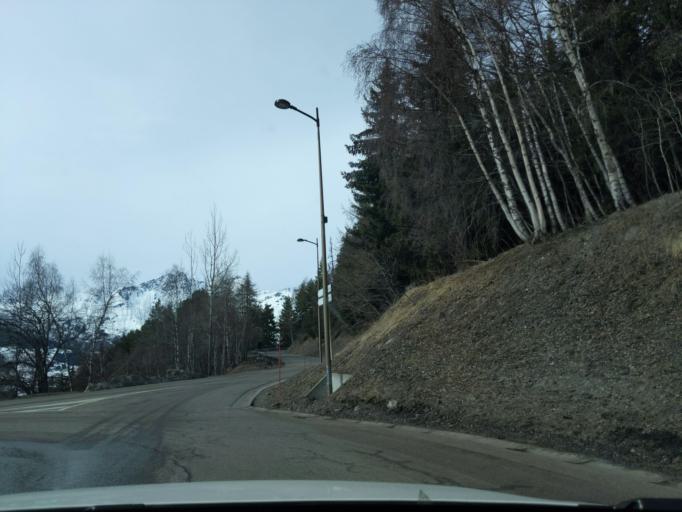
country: FR
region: Rhone-Alpes
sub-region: Departement de la Savoie
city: Seez
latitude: 45.5929
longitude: 6.7903
